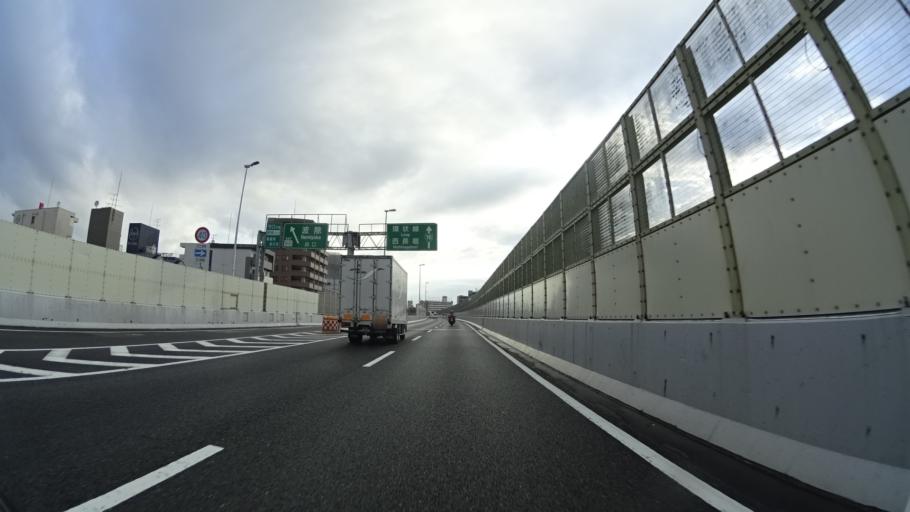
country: JP
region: Osaka
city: Osaka-shi
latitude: 34.6690
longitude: 135.4634
